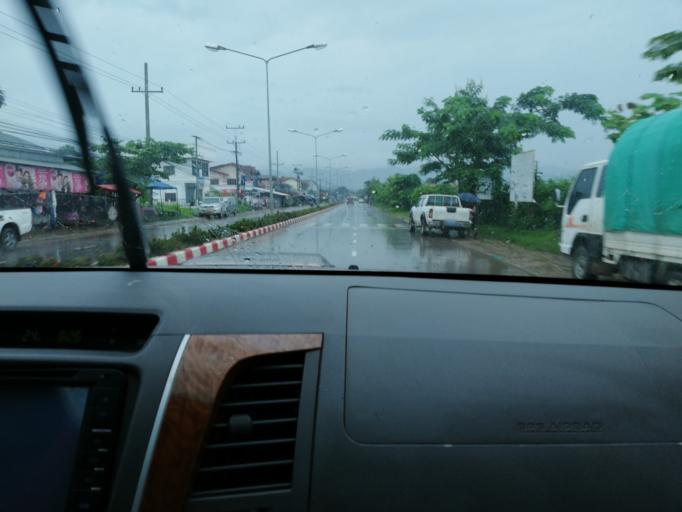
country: LA
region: Loungnamtha
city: Louang Namtha
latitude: 20.9531
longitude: 101.4035
